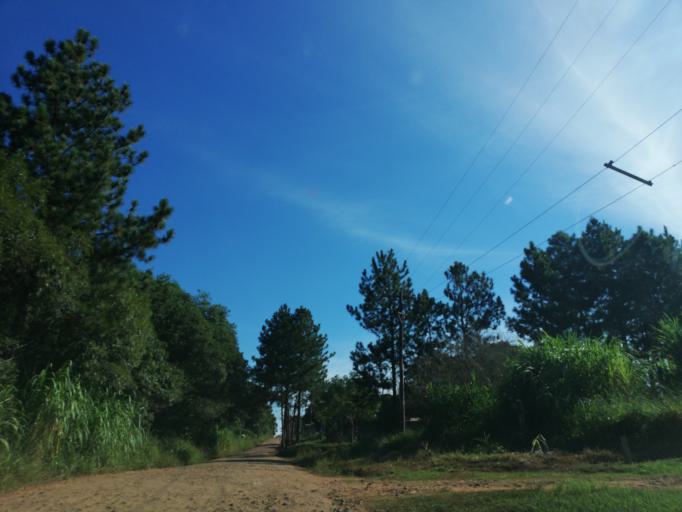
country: AR
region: Misiones
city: Dos de Mayo
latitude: -27.0161
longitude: -54.4543
